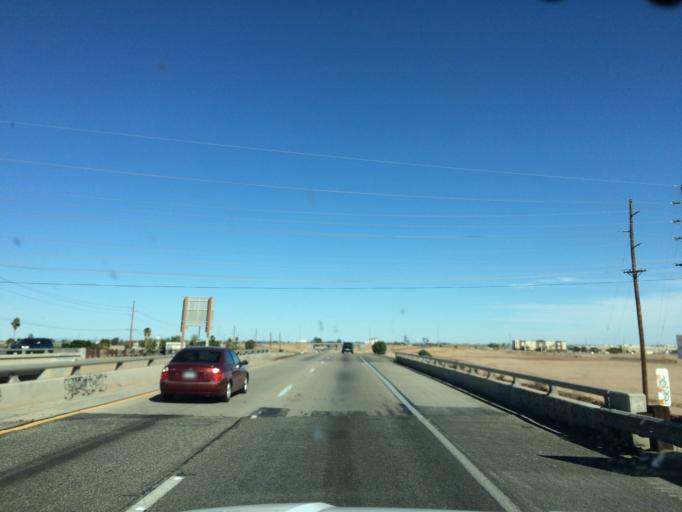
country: US
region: California
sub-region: Imperial County
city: El Centro
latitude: 32.7736
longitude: -115.5437
